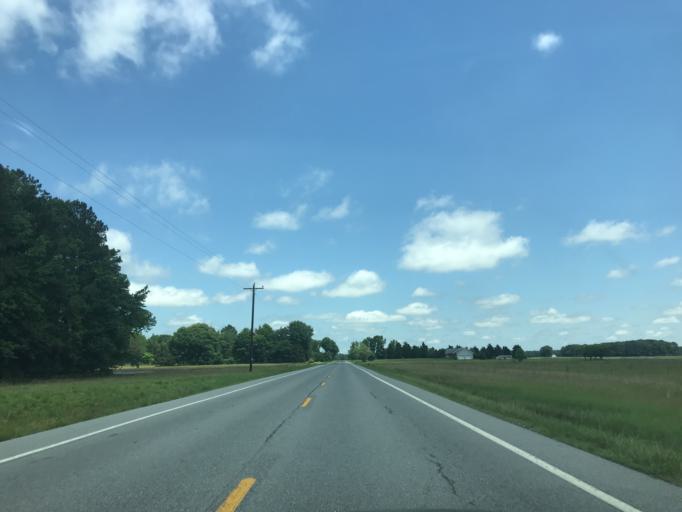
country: US
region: Maryland
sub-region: Caroline County
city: Federalsburg
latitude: 38.7167
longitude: -75.7404
